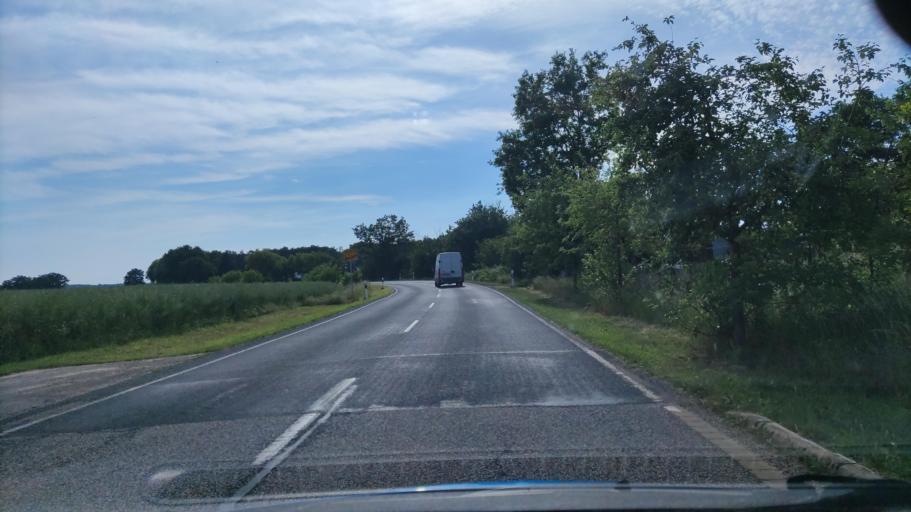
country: DE
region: Saxony-Anhalt
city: Klotze
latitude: 52.6760
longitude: 11.2127
